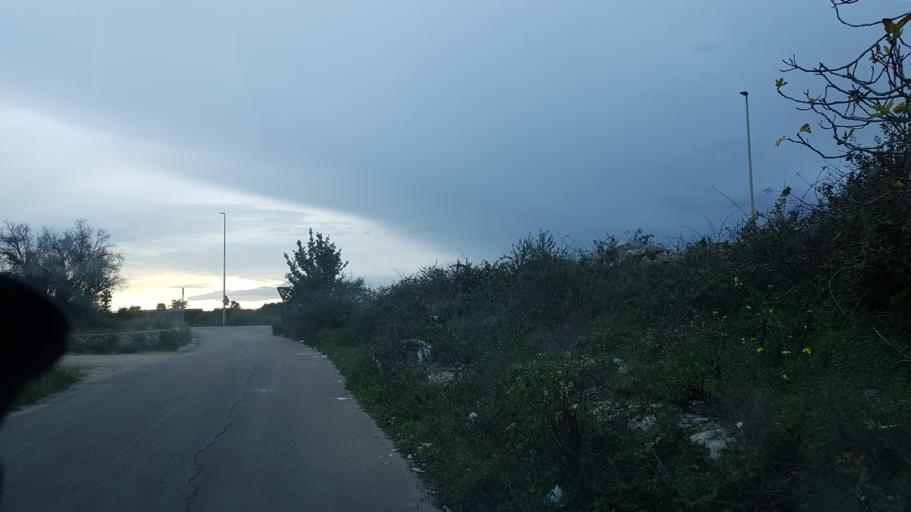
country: IT
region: Apulia
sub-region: Provincia di Lecce
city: Merine
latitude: 40.3251
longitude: 18.2239
